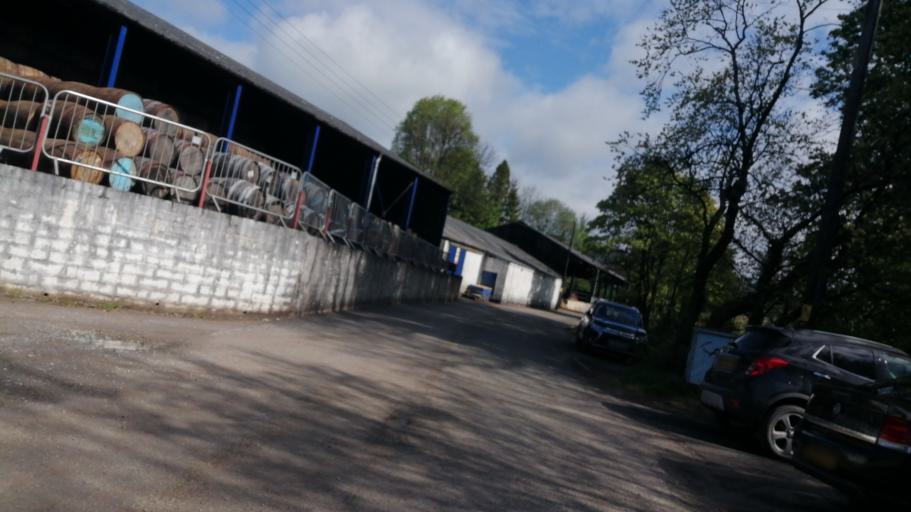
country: GB
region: Scotland
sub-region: Moray
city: Keith
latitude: 57.5424
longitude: -2.9603
